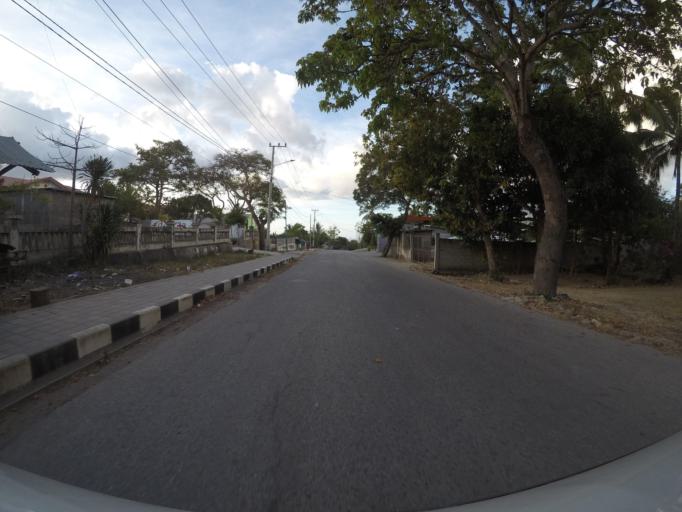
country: TL
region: Baucau
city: Baucau
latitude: -8.4690
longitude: 126.4591
